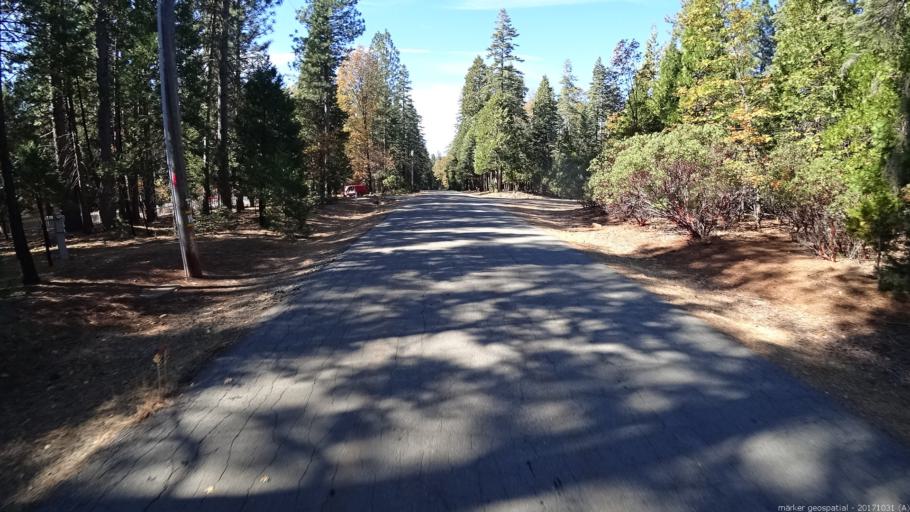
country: US
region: California
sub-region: Shasta County
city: Shingletown
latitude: 40.4853
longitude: -121.8955
